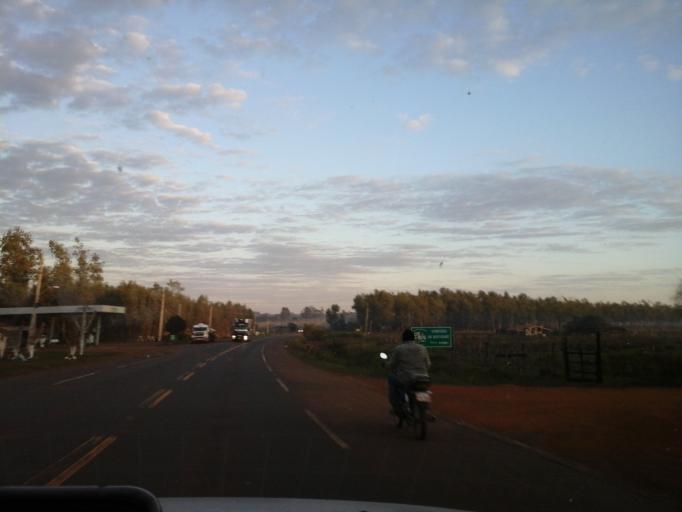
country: PY
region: Misiones
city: Santiago
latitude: -27.0433
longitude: -56.6578
